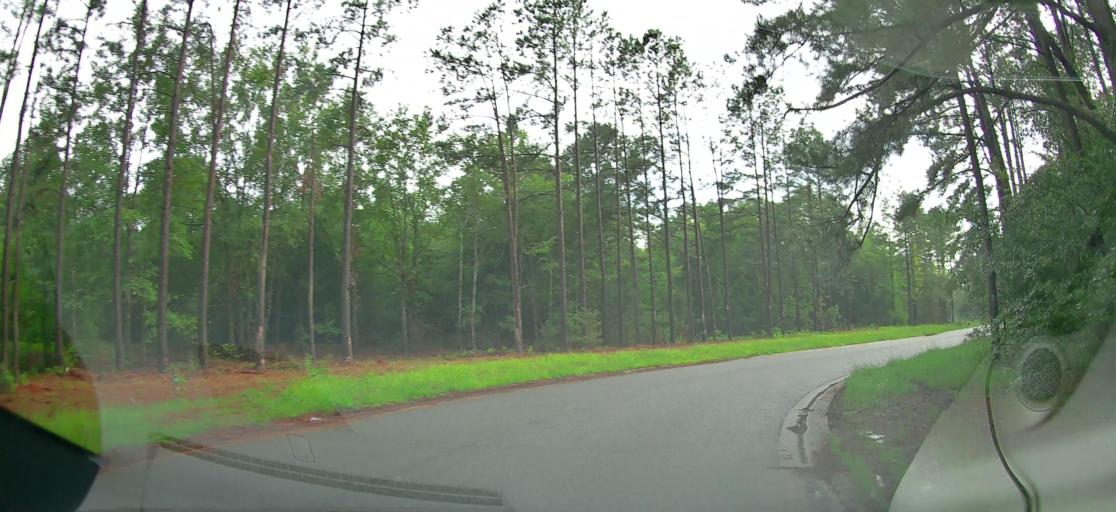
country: US
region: Georgia
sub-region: Houston County
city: Centerville
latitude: 32.6506
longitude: -83.6993
